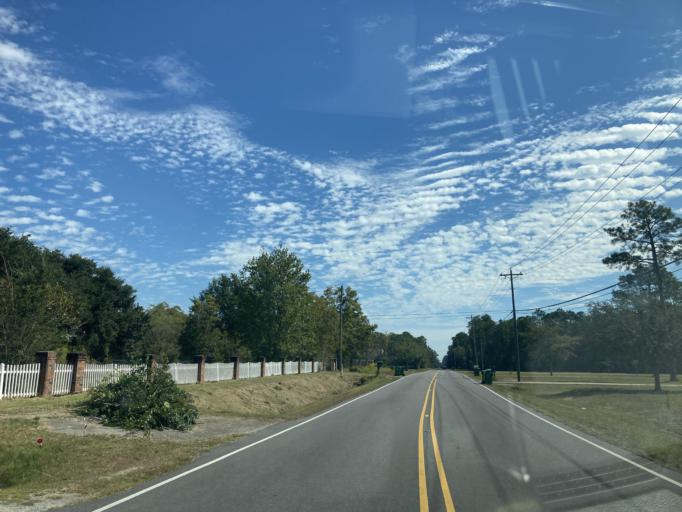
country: US
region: Mississippi
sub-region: Jackson County
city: Saint Martin
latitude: 30.4503
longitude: -88.8621
